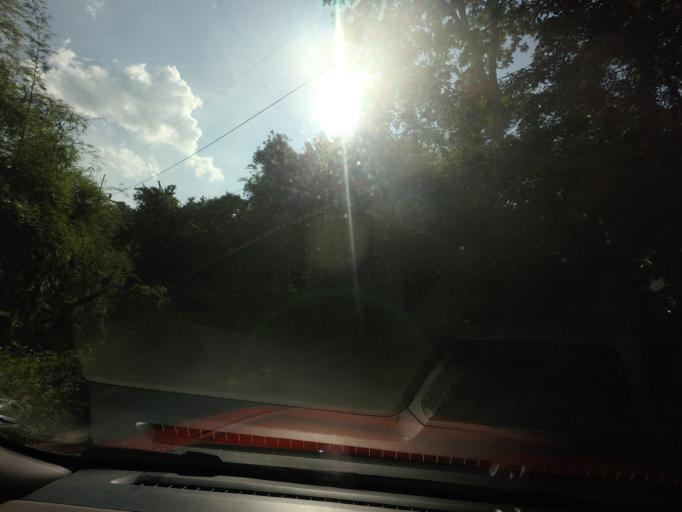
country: TH
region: Narathiwat
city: Si Sakhon
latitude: 6.0688
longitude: 101.3681
